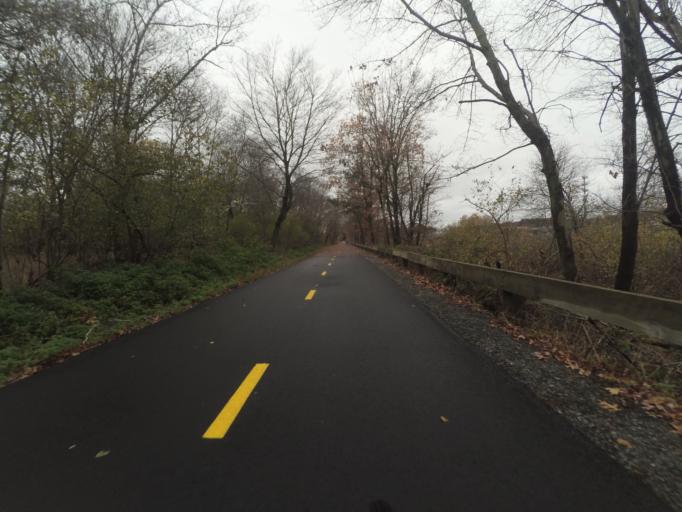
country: US
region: Massachusetts
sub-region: Middlesex County
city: Bedford
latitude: 42.4697
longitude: -71.2543
